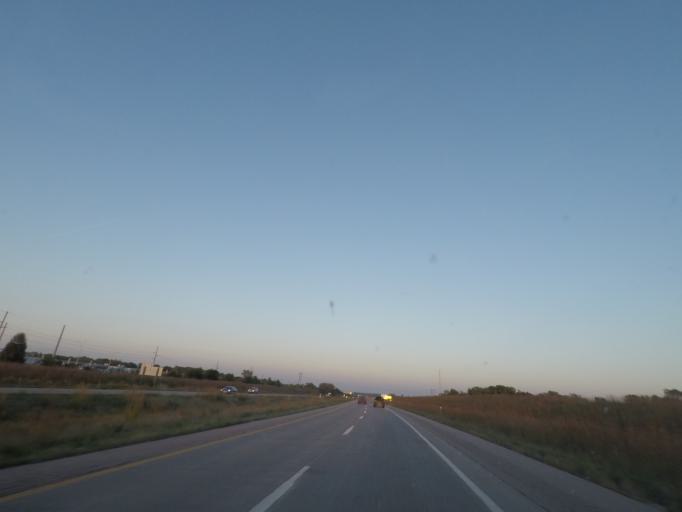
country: US
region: Iowa
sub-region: Warren County
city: Norwalk
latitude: 41.5133
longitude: -93.7065
